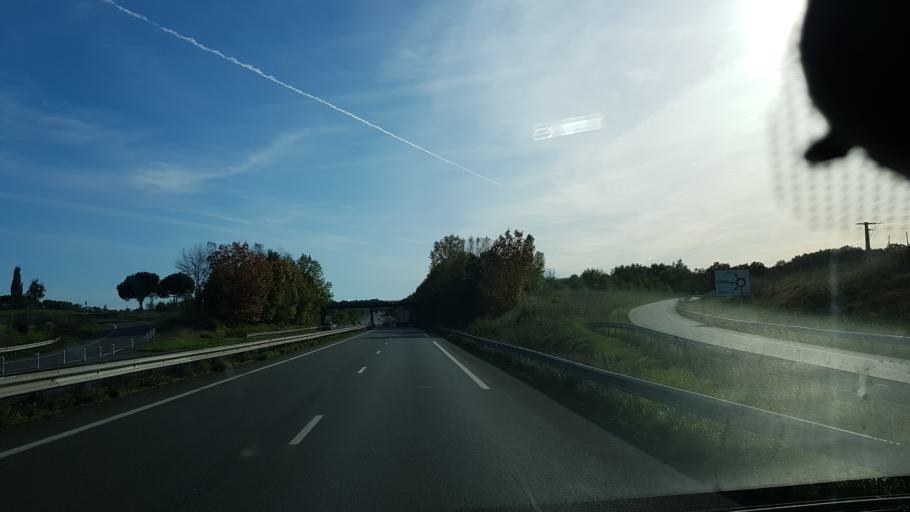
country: FR
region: Poitou-Charentes
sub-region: Departement de la Charente-Maritime
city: Chevanceaux
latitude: 45.2944
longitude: -0.2405
